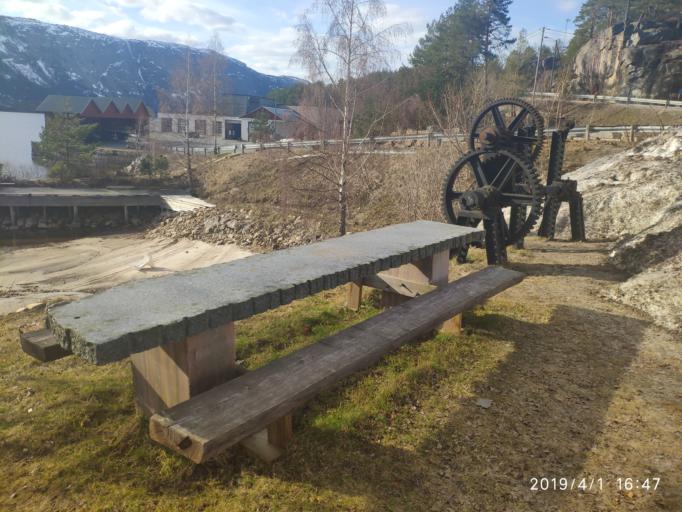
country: NO
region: Telemark
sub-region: Nissedal
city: Treungen
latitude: 59.0202
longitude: 8.5200
